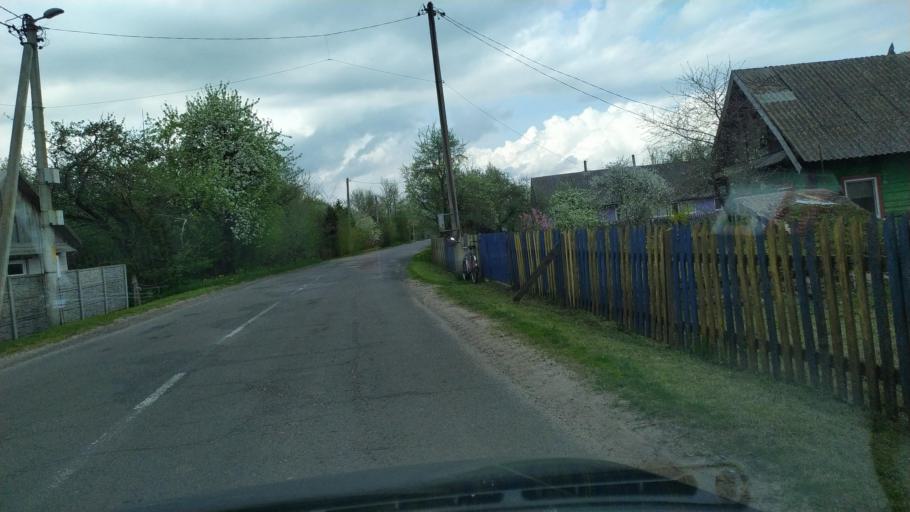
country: BY
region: Brest
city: Pruzhany
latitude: 52.6242
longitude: 24.3901
